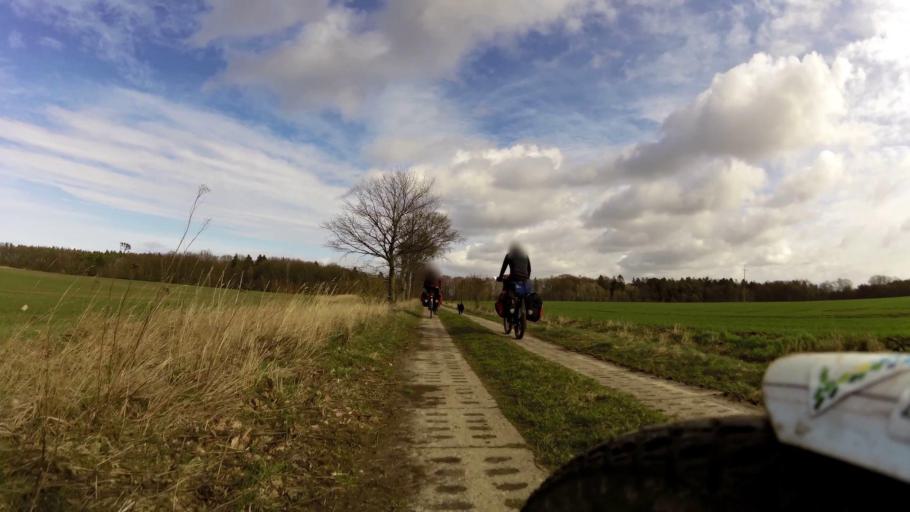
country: PL
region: West Pomeranian Voivodeship
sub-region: Powiat kamienski
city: Dziwnow
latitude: 54.0016
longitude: 14.7855
